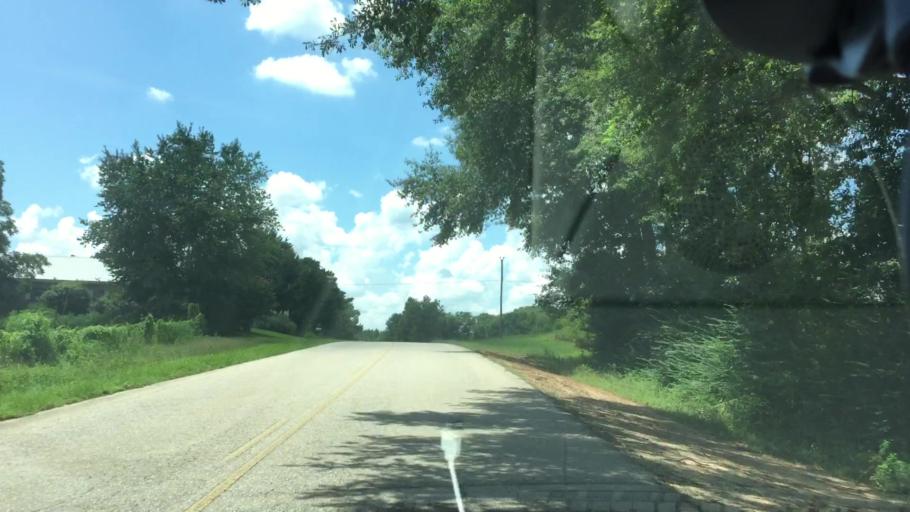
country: US
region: Alabama
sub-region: Pike County
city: Troy
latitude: 31.7471
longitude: -85.9688
